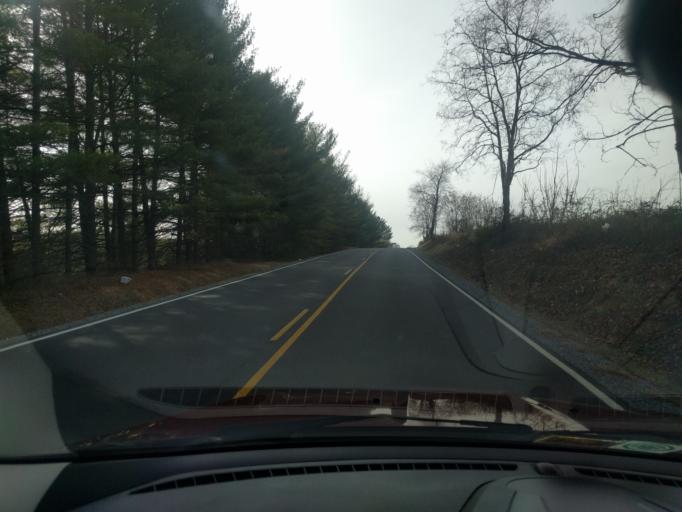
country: US
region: Virginia
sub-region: Augusta County
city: Stuarts Draft
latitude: 38.0345
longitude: -79.1160
